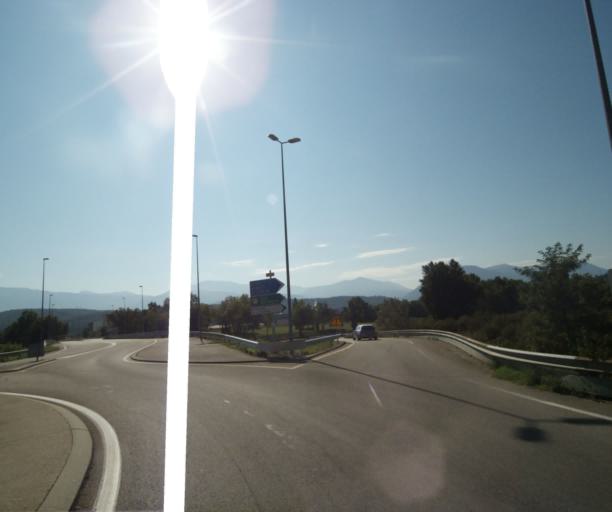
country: FR
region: Rhone-Alpes
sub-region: Departement de l'Isere
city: Claix
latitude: 45.1359
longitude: 5.6892
